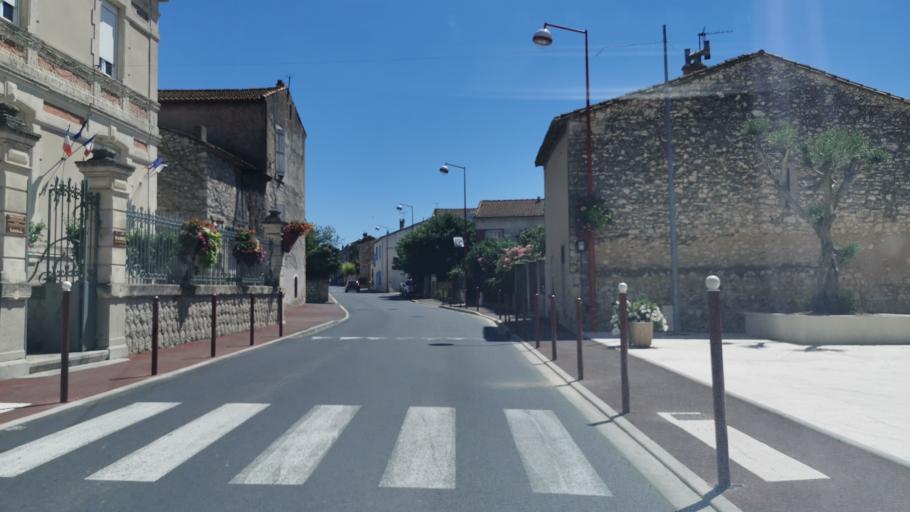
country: FR
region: Languedoc-Roussillon
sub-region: Departement de l'Aude
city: Vinassan
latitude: 43.2027
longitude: 3.0744
